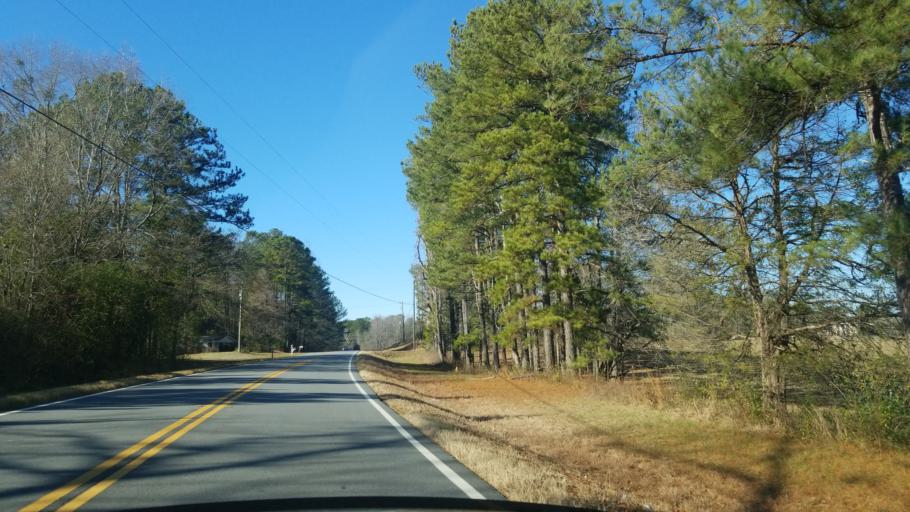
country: US
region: Georgia
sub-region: Harris County
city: Hamilton
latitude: 32.6712
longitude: -84.9046
